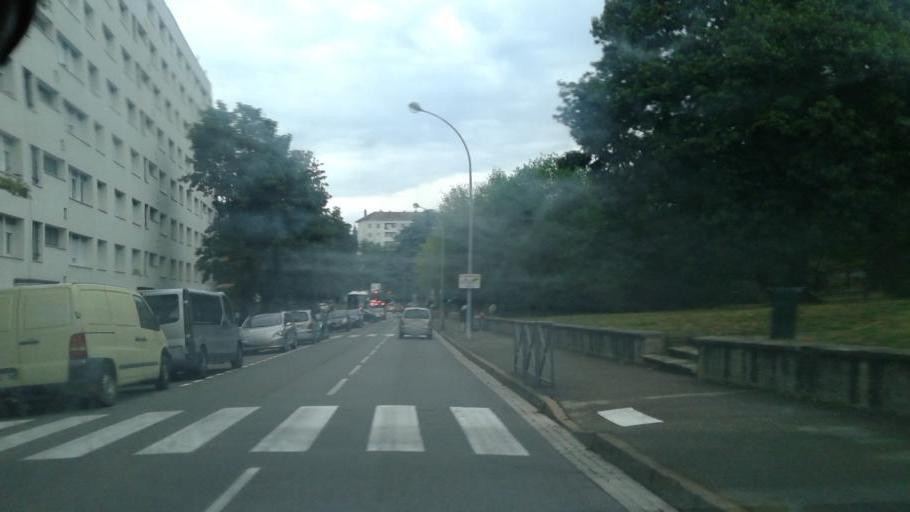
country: FR
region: Rhone-Alpes
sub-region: Departement du Rhone
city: Rillieux-la-Pape
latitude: 45.8218
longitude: 4.8960
